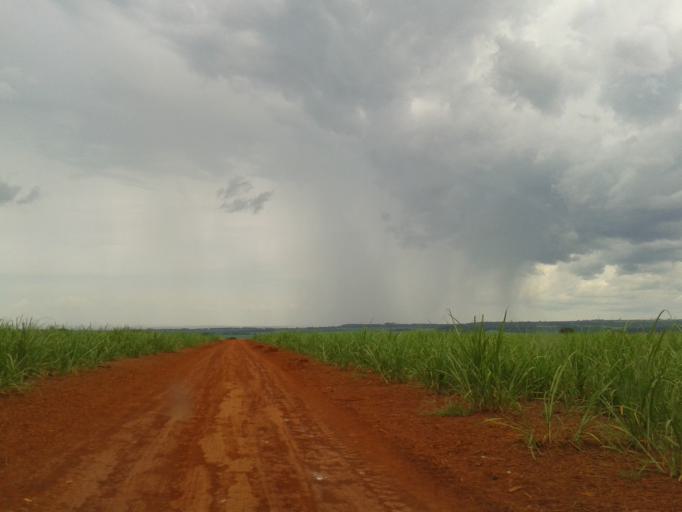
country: BR
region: Minas Gerais
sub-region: Centralina
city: Centralina
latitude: -18.6676
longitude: -49.2607
